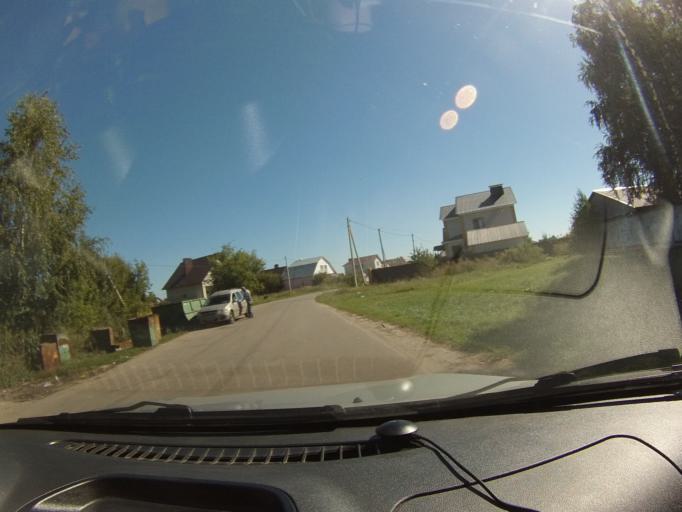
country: RU
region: Tambov
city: Komsomolets
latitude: 52.7662
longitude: 41.3624
